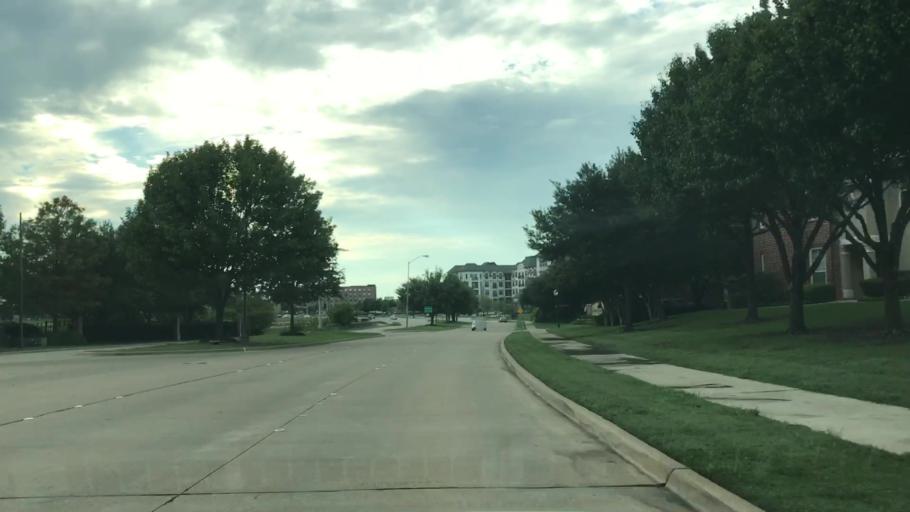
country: US
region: Texas
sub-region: Collin County
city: Frisco
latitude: 33.0876
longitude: -96.7997
